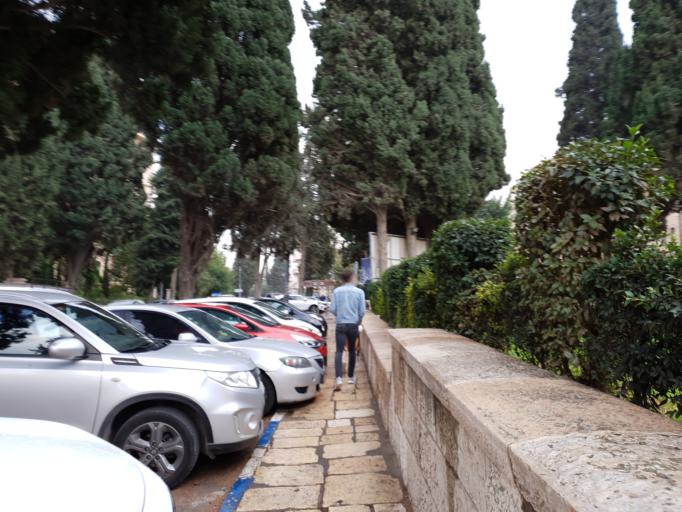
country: IL
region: Jerusalem
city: West Jerusalem
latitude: 31.7747
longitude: 35.2219
